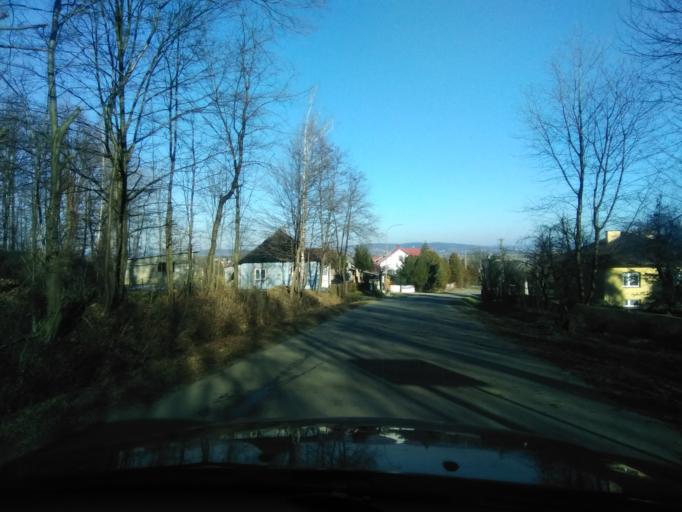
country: PL
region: Subcarpathian Voivodeship
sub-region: Powiat krosnienski
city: Rymanow
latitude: 49.6009
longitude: 21.8972
